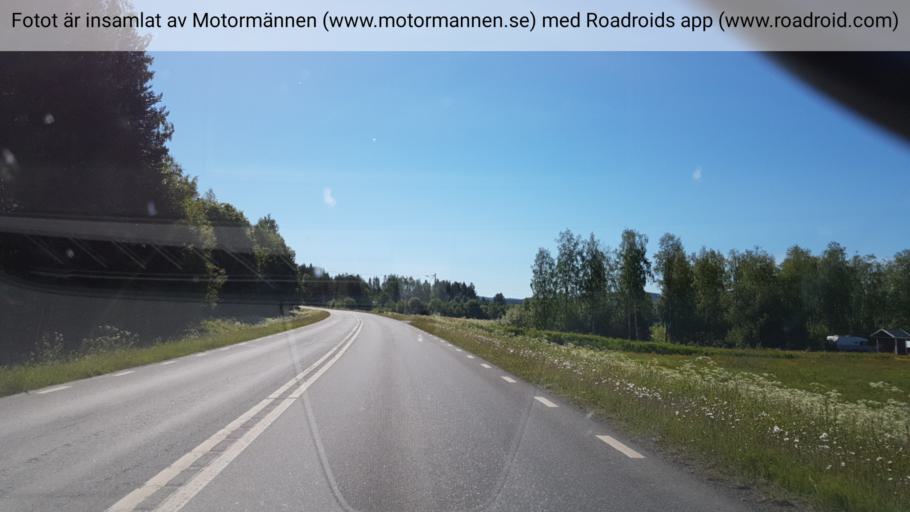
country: SE
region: Norrbotten
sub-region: Bodens Kommun
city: Boden
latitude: 65.8654
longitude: 21.4182
